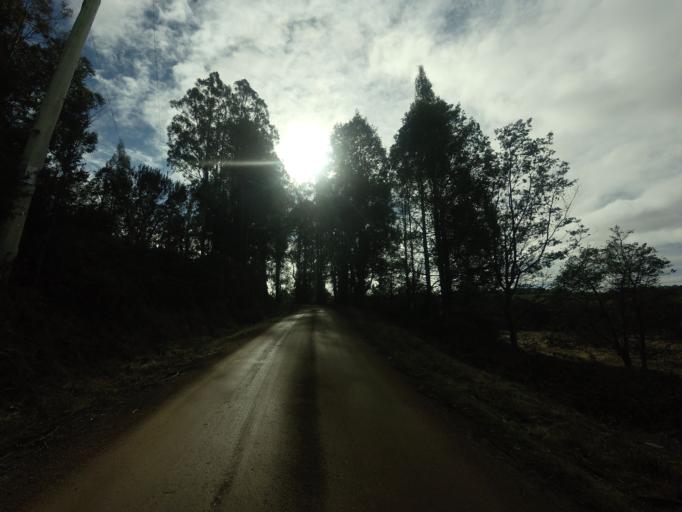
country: AU
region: Tasmania
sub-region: Derwent Valley
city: New Norfolk
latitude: -42.7886
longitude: 146.9181
